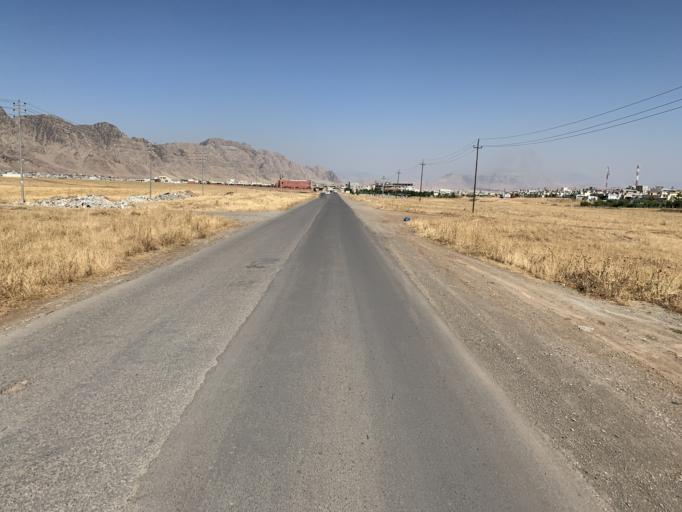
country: IQ
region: As Sulaymaniyah
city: Raniye
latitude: 36.2634
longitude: 44.8484
